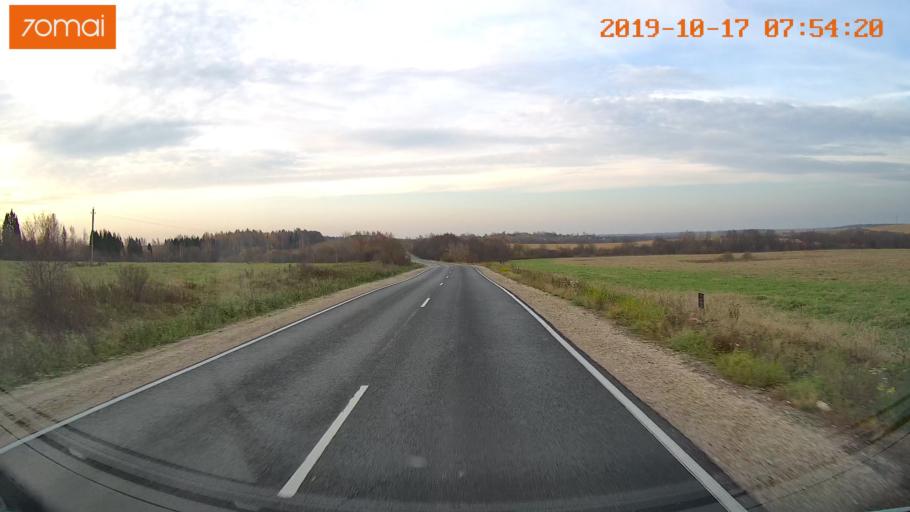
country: RU
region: Vladimir
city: Bavleny
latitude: 56.4510
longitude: 39.6073
